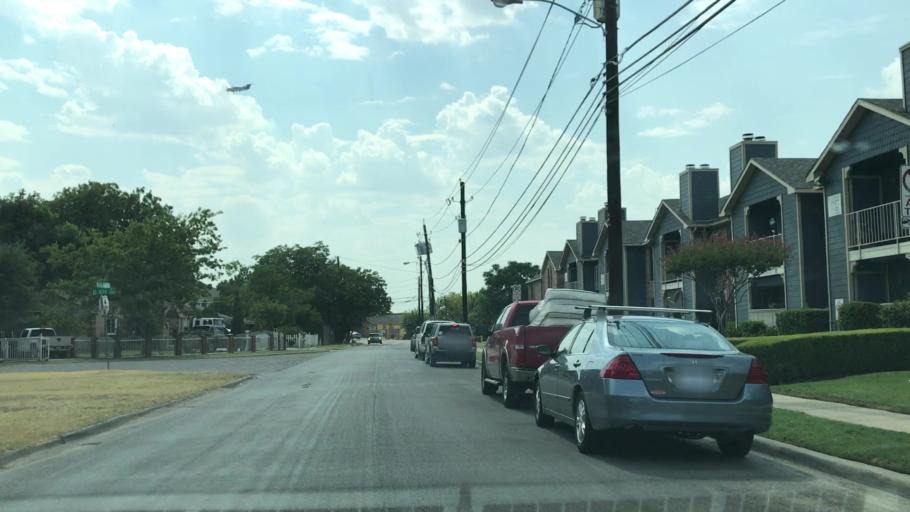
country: US
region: Texas
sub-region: Dallas County
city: University Park
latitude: 32.8653
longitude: -96.8604
